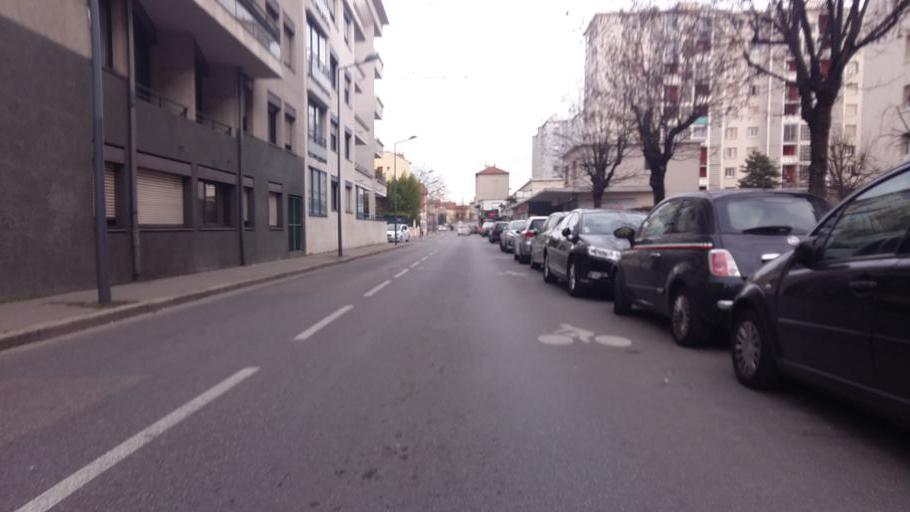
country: FR
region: Rhone-Alpes
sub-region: Departement du Rhone
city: Villeurbanne
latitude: 45.7714
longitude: 4.8833
